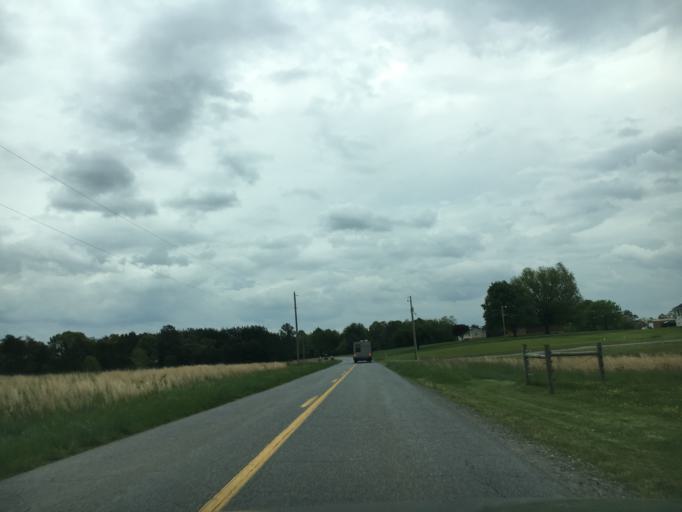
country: US
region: Virginia
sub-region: Campbell County
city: Rustburg
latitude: 37.2167
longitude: -79.0433
